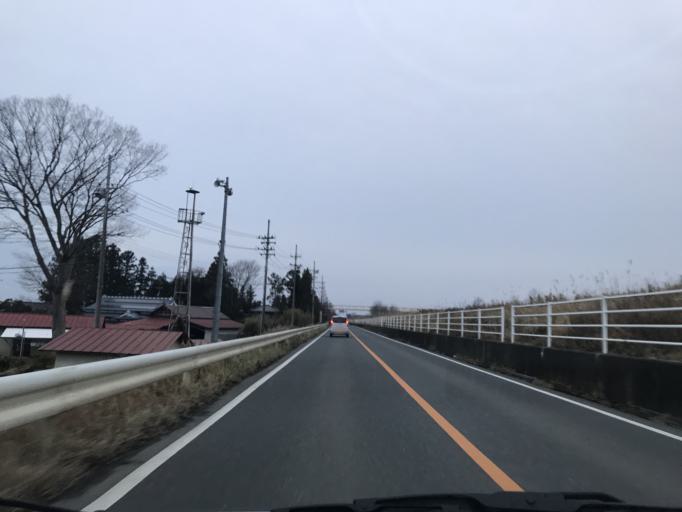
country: JP
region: Iwate
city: Ichinoseki
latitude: 38.7531
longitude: 141.1421
